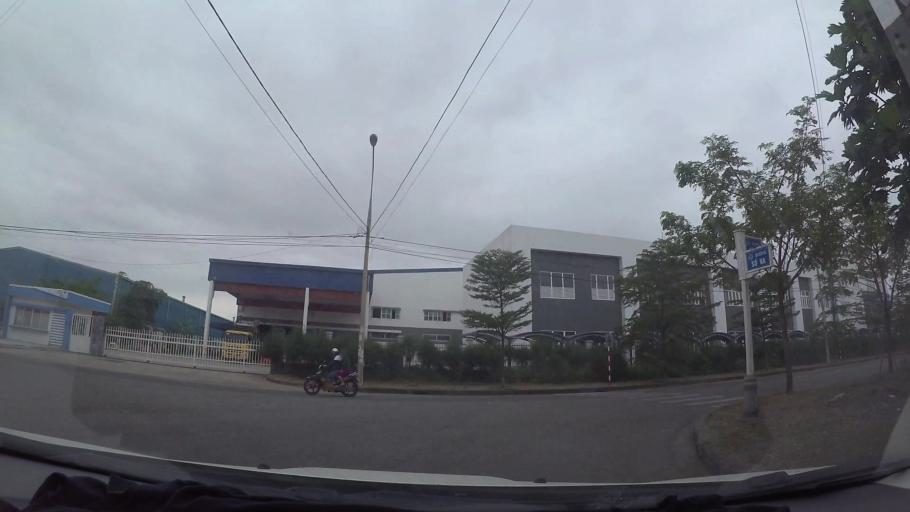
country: VN
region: Da Nang
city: Lien Chieu
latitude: 16.0875
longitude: 108.1371
